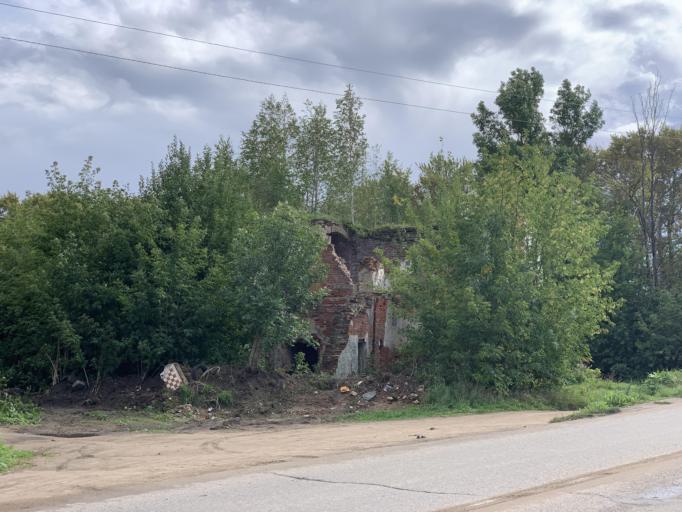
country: RU
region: Tverskaya
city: Vyshniy Volochek
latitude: 57.5794
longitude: 34.5580
